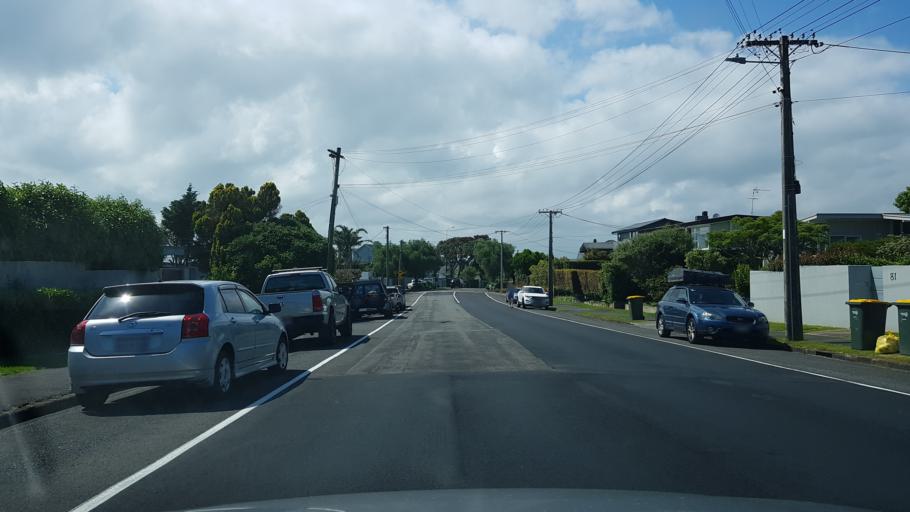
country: NZ
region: Auckland
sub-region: Auckland
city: North Shore
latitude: -36.8086
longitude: 174.7972
